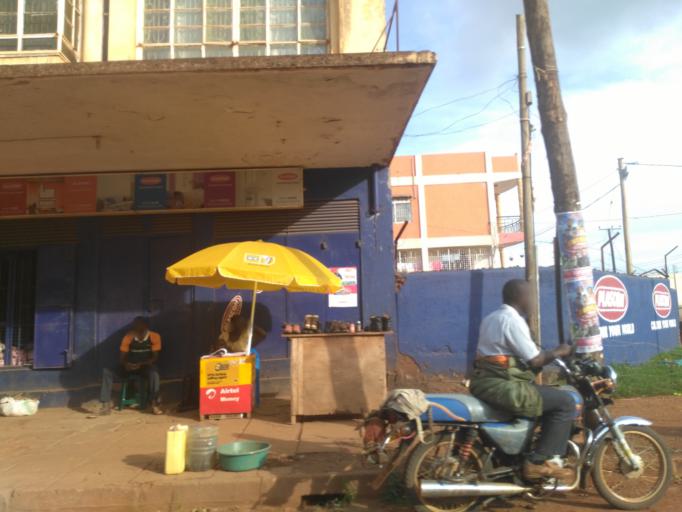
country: UG
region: Eastern Region
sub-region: Jinja District
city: Jinja
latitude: 0.4280
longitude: 33.2111
